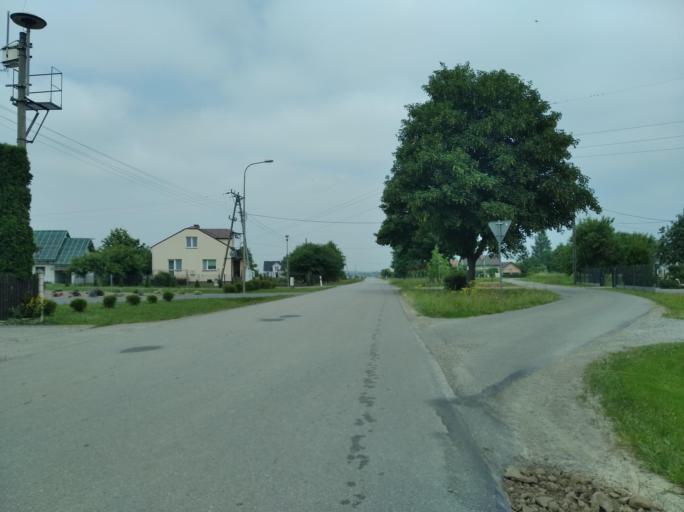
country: PL
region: Subcarpathian Voivodeship
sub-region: Powiat sanocki
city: Besko
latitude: 49.5981
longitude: 21.9597
